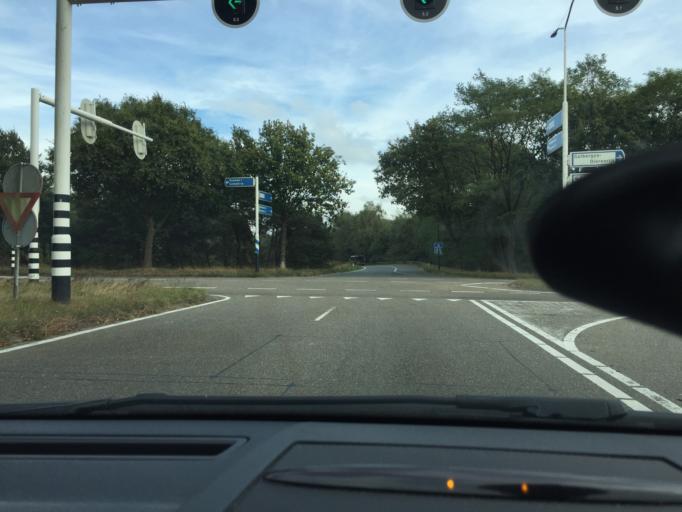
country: NL
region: North Brabant
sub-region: Gemeente Nuenen, Gerwen en Nederwetten
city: Nuenen
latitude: 51.4597
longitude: 5.5592
